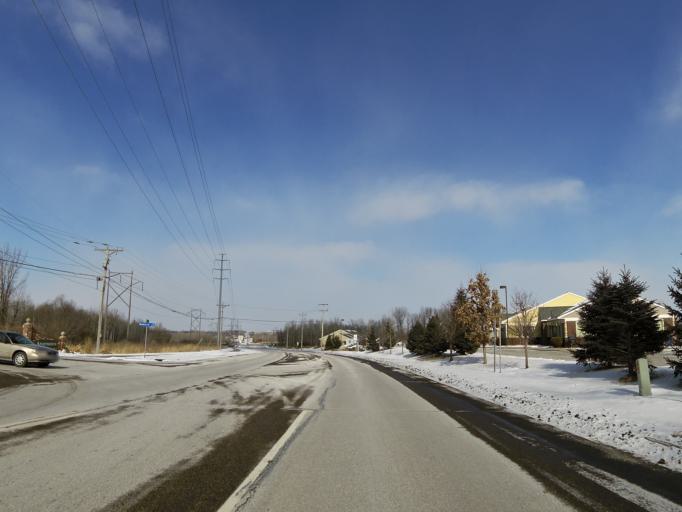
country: US
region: Minnesota
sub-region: Washington County
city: Woodbury
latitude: 44.9309
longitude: -92.9646
